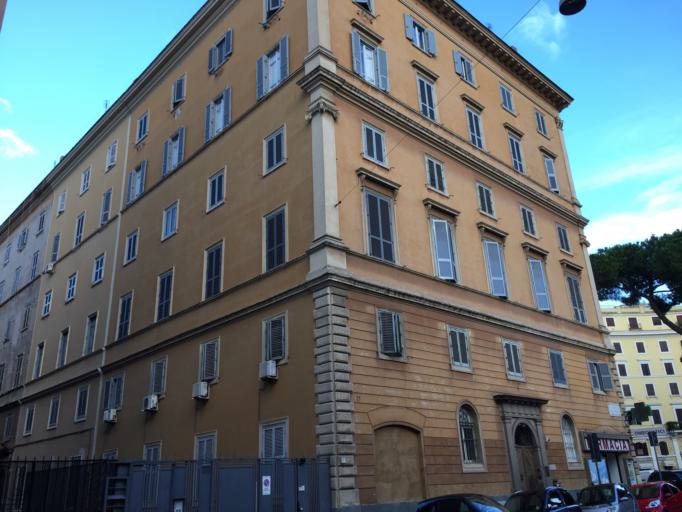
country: VA
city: Vatican City
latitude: 41.9086
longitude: 12.4647
